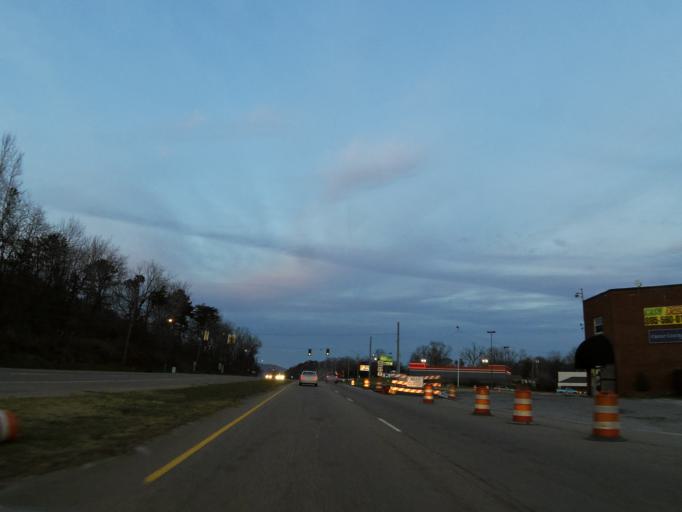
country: US
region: Tennessee
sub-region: Roane County
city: Harriman
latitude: 35.9201
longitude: -84.5647
